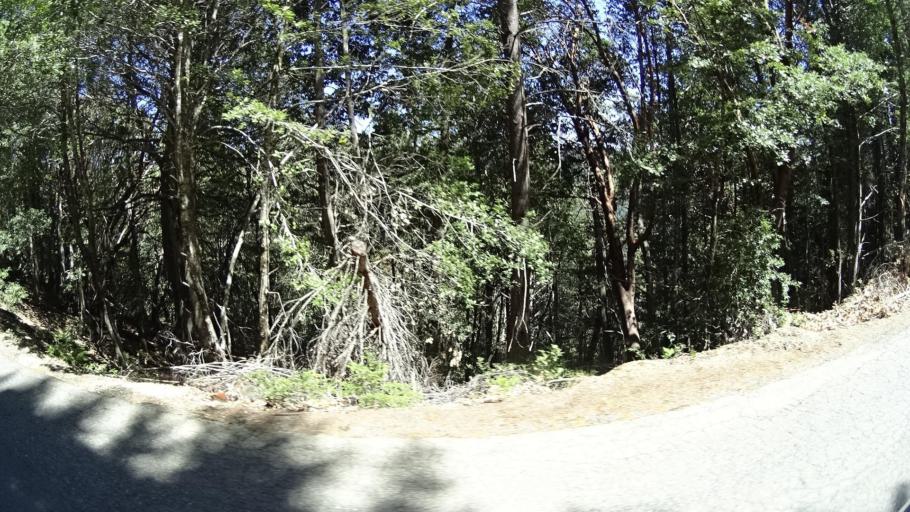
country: US
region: California
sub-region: Humboldt County
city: Rio Dell
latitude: 40.2702
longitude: -124.0778
